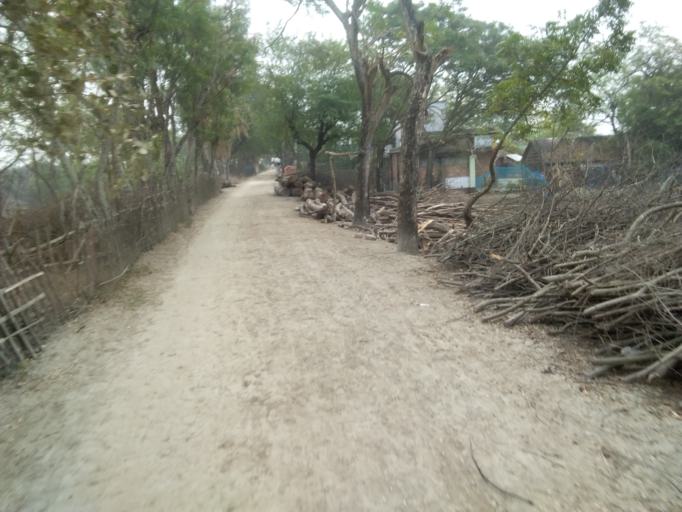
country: BD
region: Khulna
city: Satkhira
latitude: 22.5709
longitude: 89.0788
